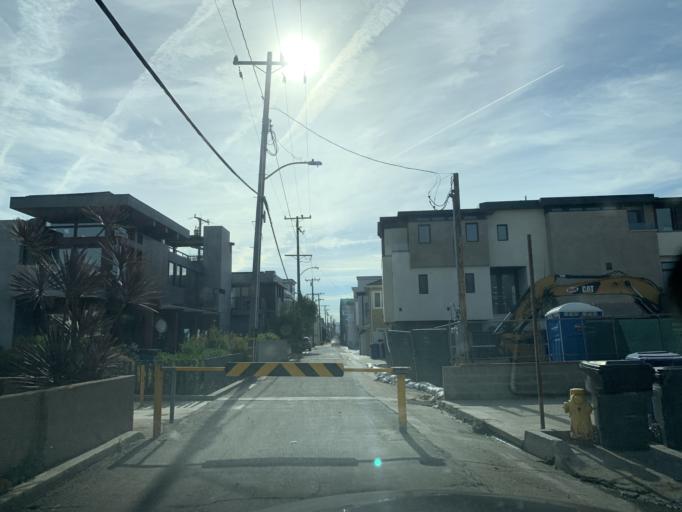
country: US
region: California
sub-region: Los Angeles County
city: Hermosa Beach
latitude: 33.8678
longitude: -118.4035
